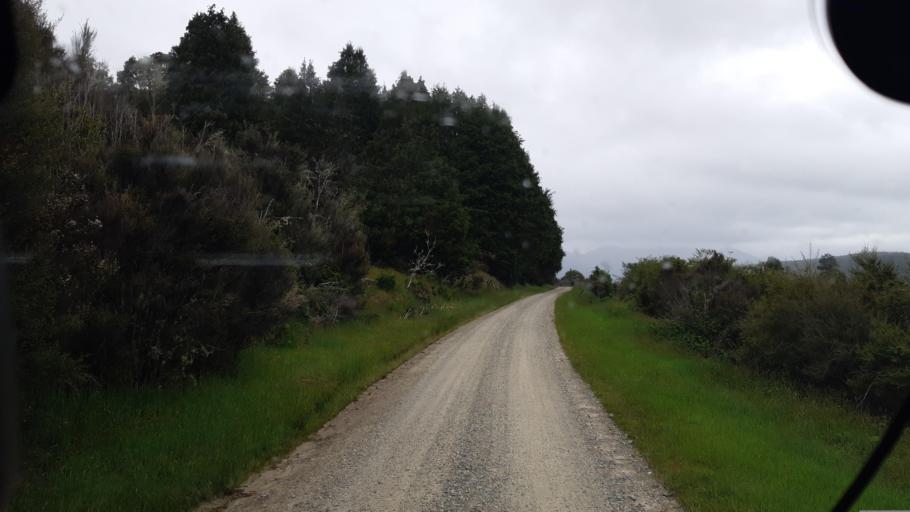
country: NZ
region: West Coast
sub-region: Buller District
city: Westport
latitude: -42.2905
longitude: 171.8201
